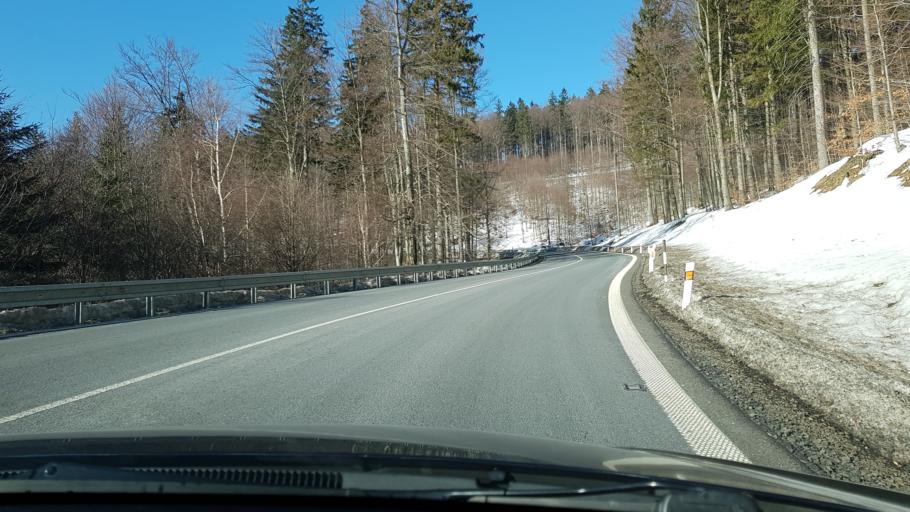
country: CZ
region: Olomoucky
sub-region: Okres Sumperk
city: Loucna nad Desnou
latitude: 50.1079
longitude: 17.1446
